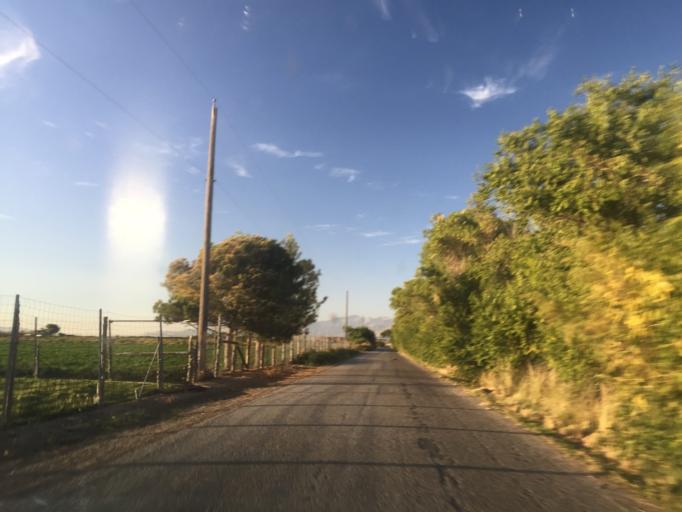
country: US
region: Utah
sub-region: Utah County
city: Benjamin
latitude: 40.1632
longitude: -111.7305
